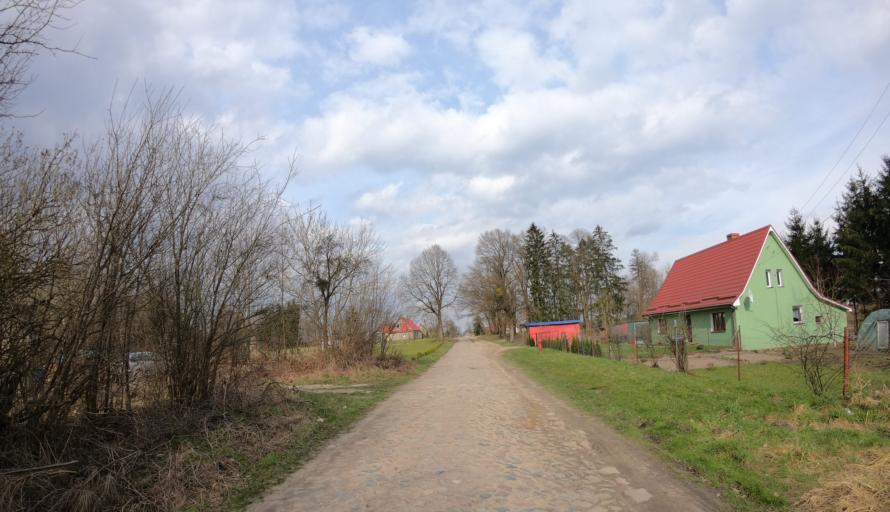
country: PL
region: West Pomeranian Voivodeship
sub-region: Powiat swidwinski
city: Rabino
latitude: 53.8767
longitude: 15.8843
